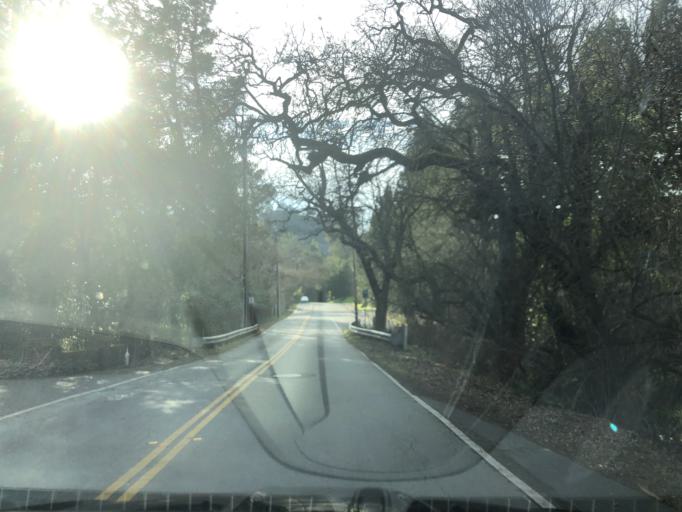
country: US
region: California
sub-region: Contra Costa County
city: Saranap
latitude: 37.8750
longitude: -122.0586
